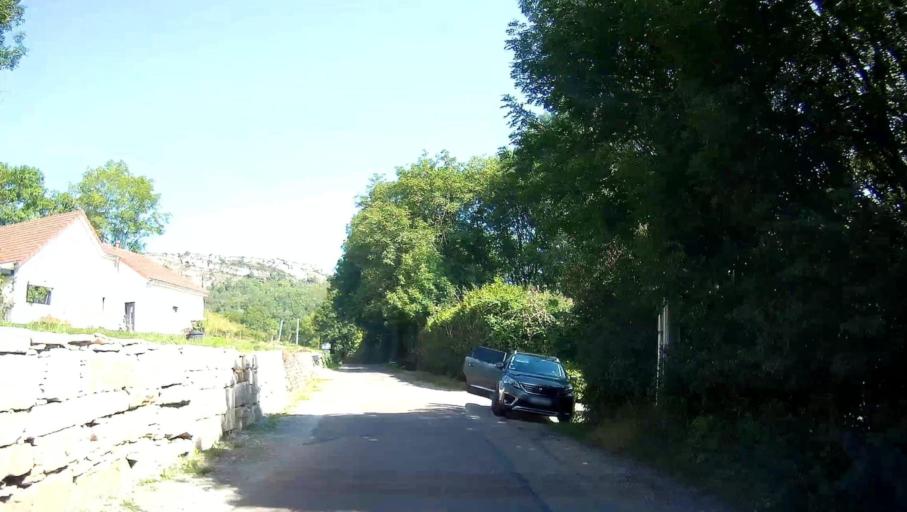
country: FR
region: Bourgogne
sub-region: Departement de la Cote-d'Or
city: Nolay
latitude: 46.9707
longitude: 4.6430
